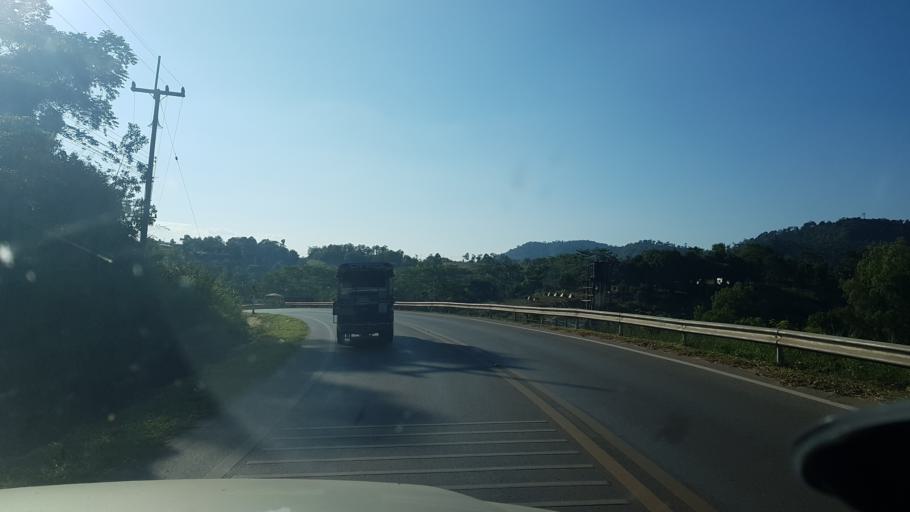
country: TH
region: Phetchabun
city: Khao Kho
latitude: 16.6479
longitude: 101.0080
